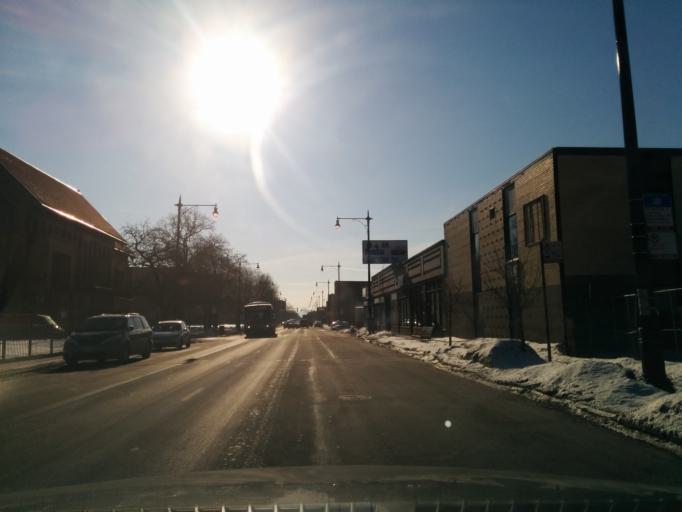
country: US
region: Illinois
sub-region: Cook County
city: Lincolnwood
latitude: 41.9477
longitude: -87.7379
